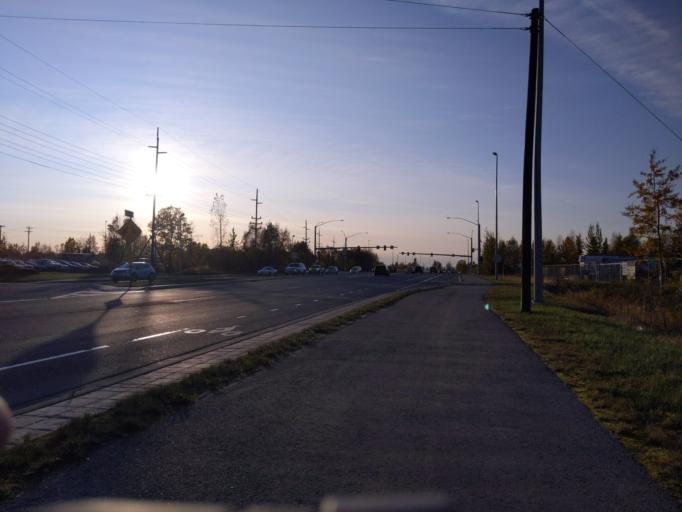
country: US
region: Alaska
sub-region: Anchorage Municipality
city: Anchorage
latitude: 61.1667
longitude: -149.8836
